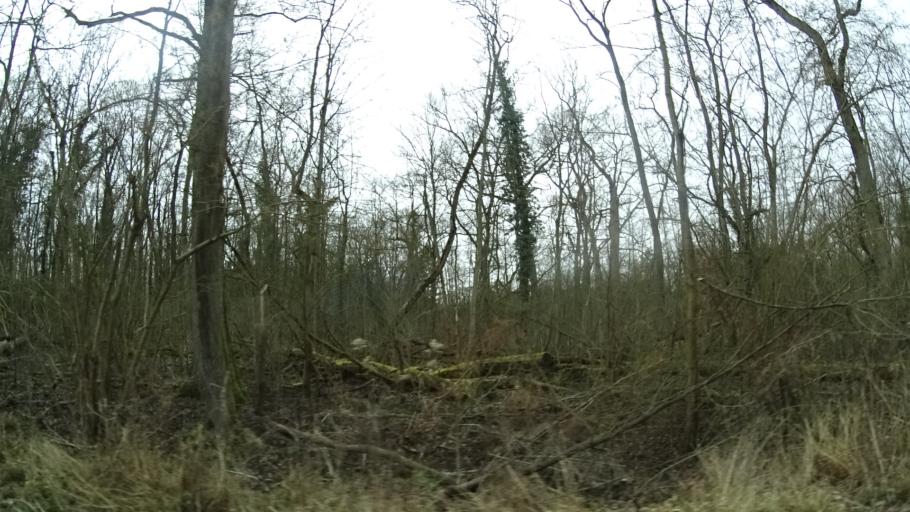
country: DE
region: Rheinland-Pfalz
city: Gimbsheim
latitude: 49.8212
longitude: 8.4019
